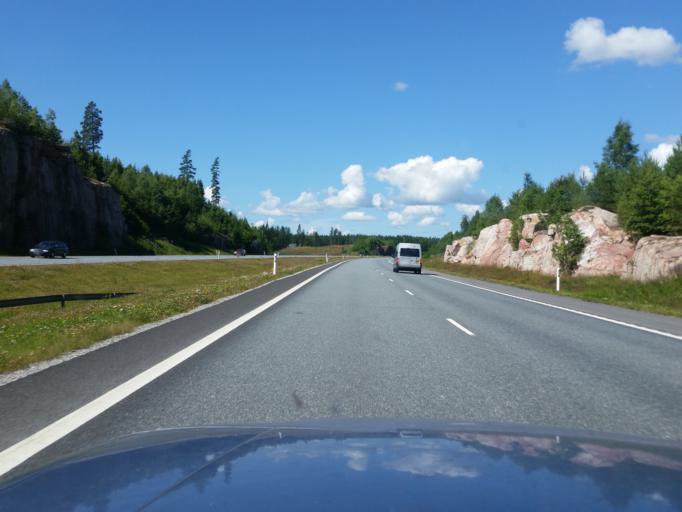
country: FI
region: Varsinais-Suomi
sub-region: Salo
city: Pertteli
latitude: 60.3992
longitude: 23.2427
